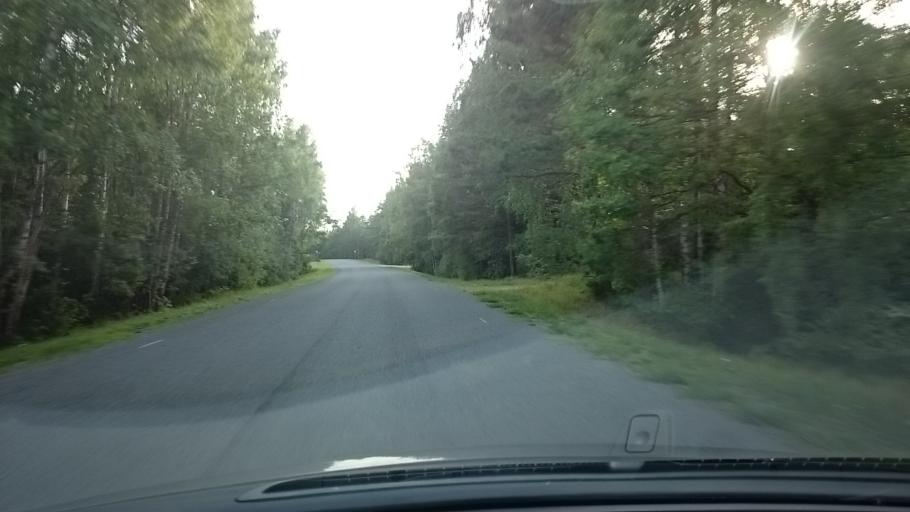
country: EE
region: Saare
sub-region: Kuressaare linn
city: Kuressaare
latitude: 58.4380
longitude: 22.2224
